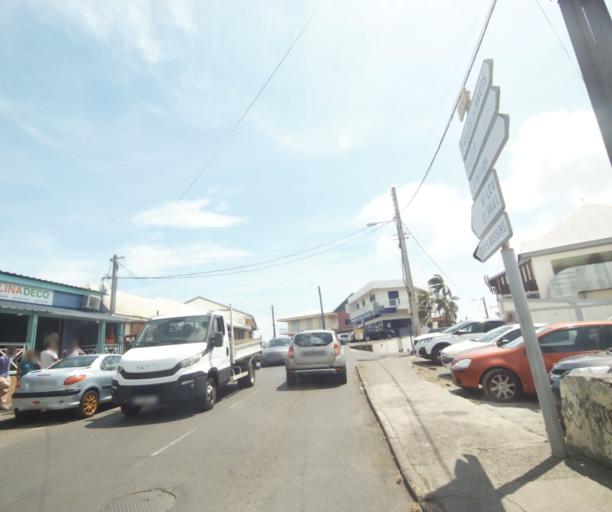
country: RE
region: Reunion
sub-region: Reunion
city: Trois-Bassins
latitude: -21.0815
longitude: 55.2705
